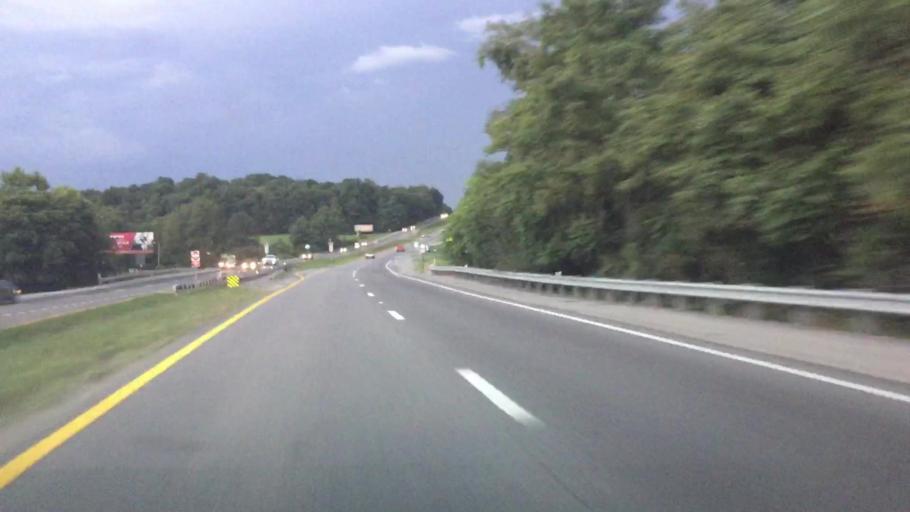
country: US
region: Virginia
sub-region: Botetourt County
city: Blue Ridge
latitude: 37.3674
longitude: -79.8184
